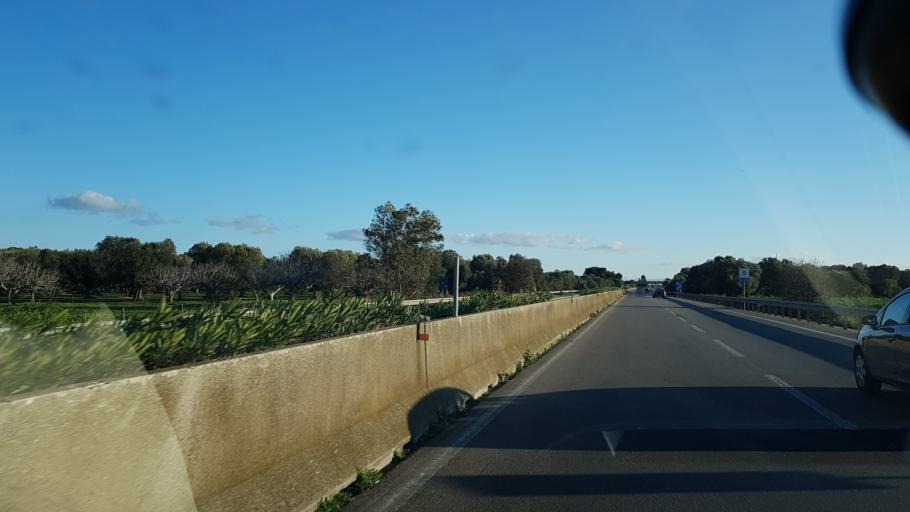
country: IT
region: Apulia
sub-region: Provincia di Brindisi
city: La Rosa
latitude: 40.5828
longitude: 17.9765
